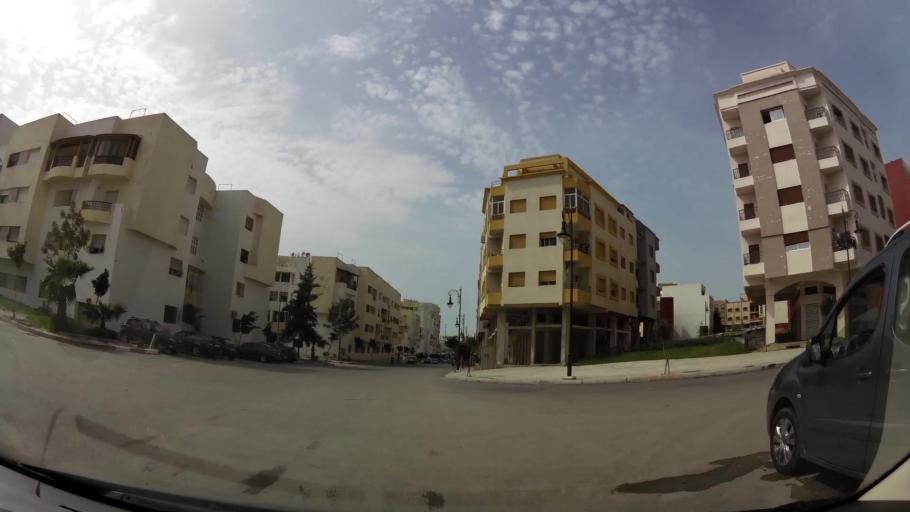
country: MA
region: Tanger-Tetouan
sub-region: Tanger-Assilah
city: Tangier
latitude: 35.7434
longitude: -5.8397
